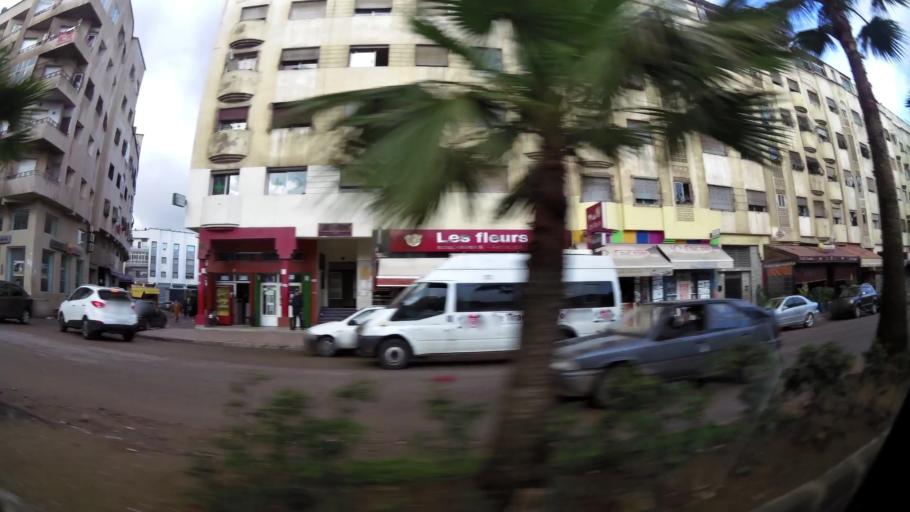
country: MA
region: Grand Casablanca
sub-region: Mediouna
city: Tit Mellil
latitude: 33.5821
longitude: -7.5245
